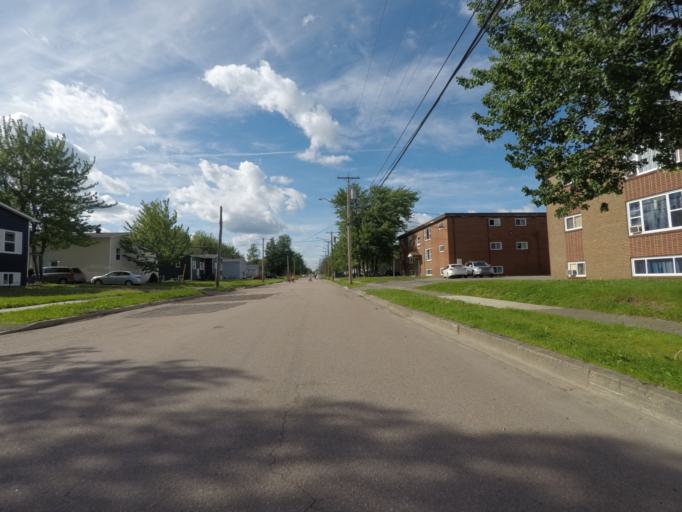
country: CA
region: New Brunswick
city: Moncton
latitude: 46.0974
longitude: -64.8219
